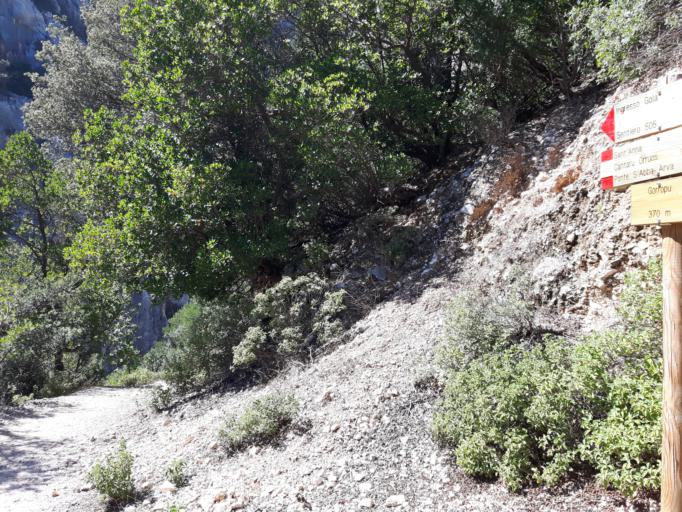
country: IT
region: Sardinia
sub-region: Provincia di Ogliastra
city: Urzulei
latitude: 40.1858
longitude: 9.5025
